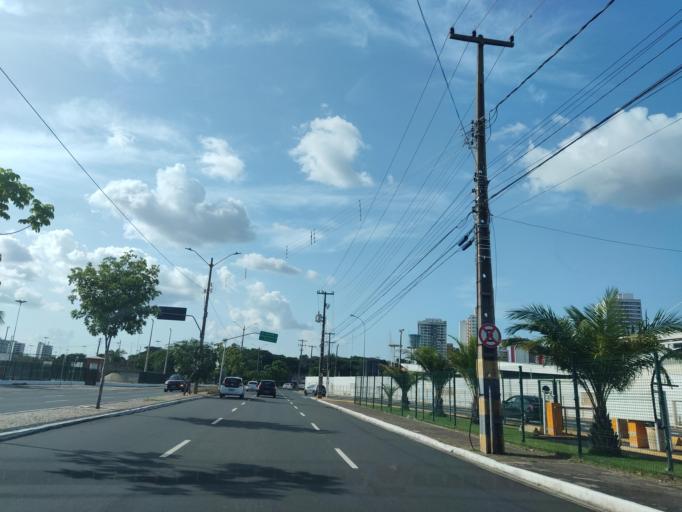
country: BR
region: Piaui
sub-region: Teresina
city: Teresina
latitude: -5.0840
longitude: -42.7922
